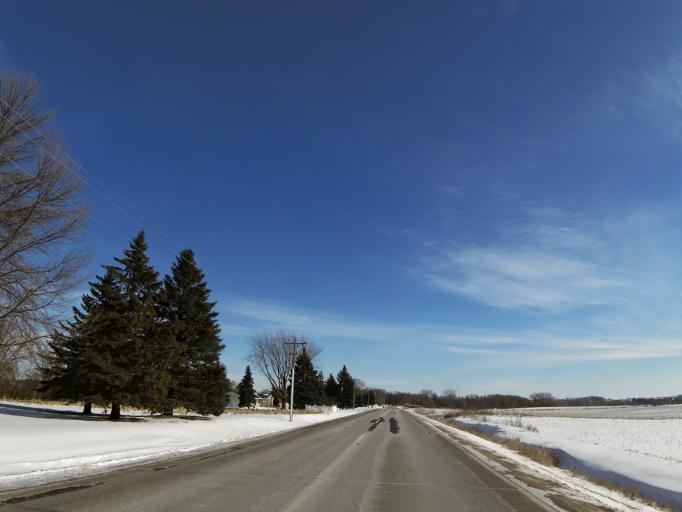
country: US
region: Minnesota
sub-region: Washington County
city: Cottage Grove
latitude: 44.7435
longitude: -92.9452
